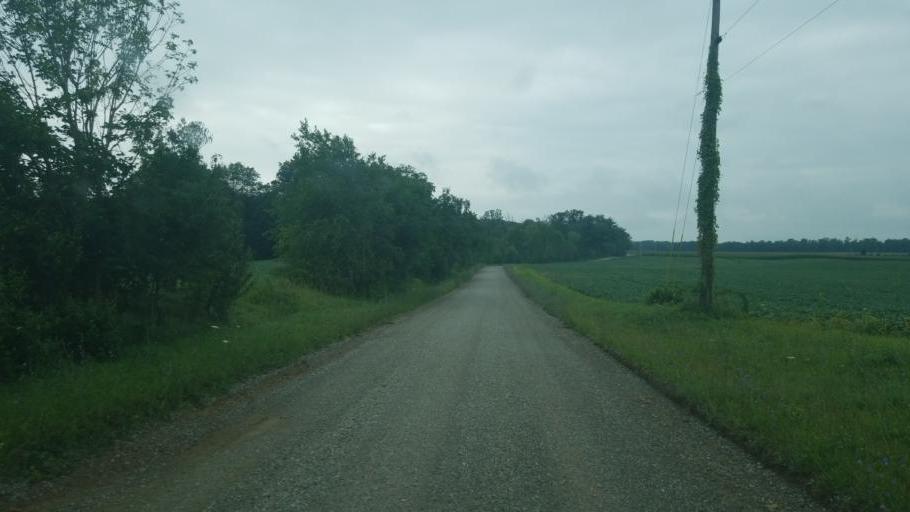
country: US
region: Ohio
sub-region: Knox County
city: Centerburg
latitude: 40.3837
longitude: -82.7421
